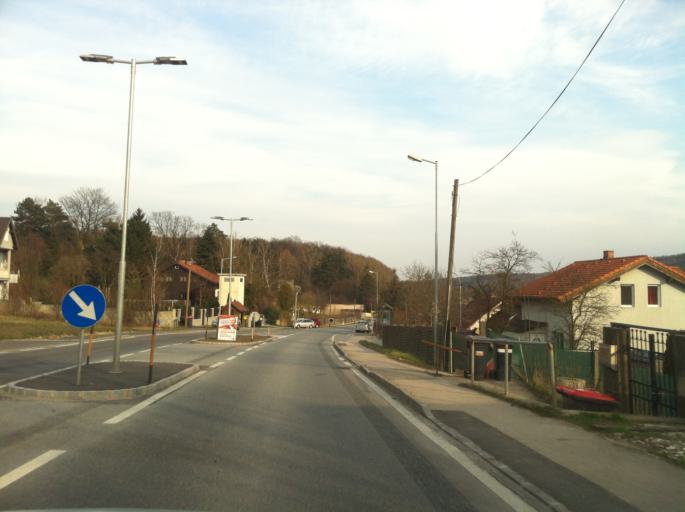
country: AT
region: Lower Austria
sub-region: Politischer Bezirk Tulln
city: Tulbing
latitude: 48.2461
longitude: 16.1060
